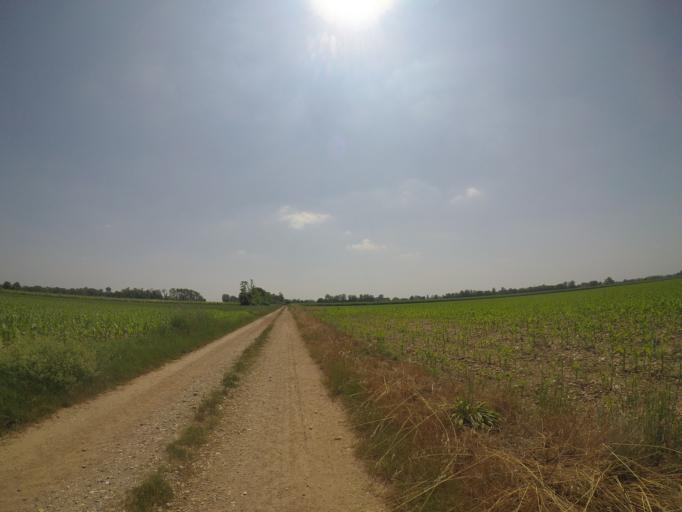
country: IT
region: Friuli Venezia Giulia
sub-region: Provincia di Udine
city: Bertiolo
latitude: 45.9711
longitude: 13.0773
